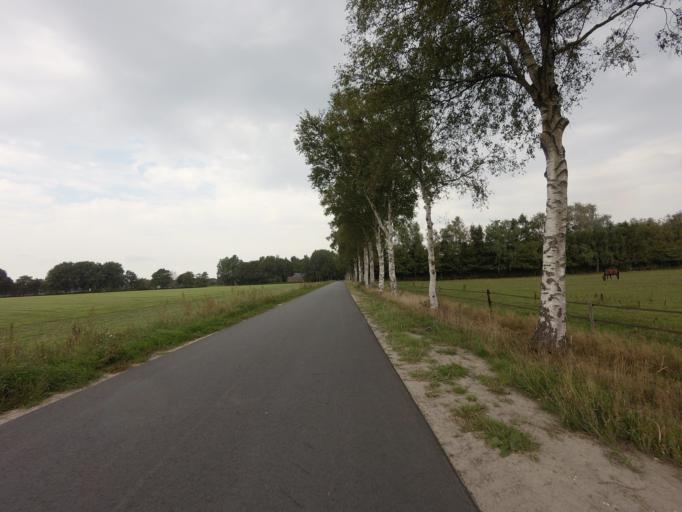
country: NL
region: Drenthe
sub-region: Gemeente Tynaarlo
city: Vries
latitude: 53.0634
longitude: 6.5839
